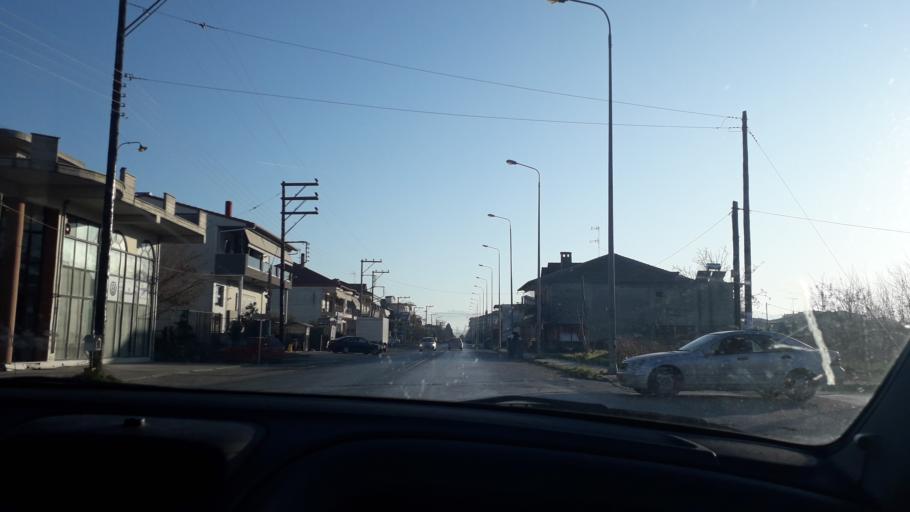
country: GR
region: Central Macedonia
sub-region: Nomos Imathias
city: Alexandreia
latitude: 40.6290
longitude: 22.4486
